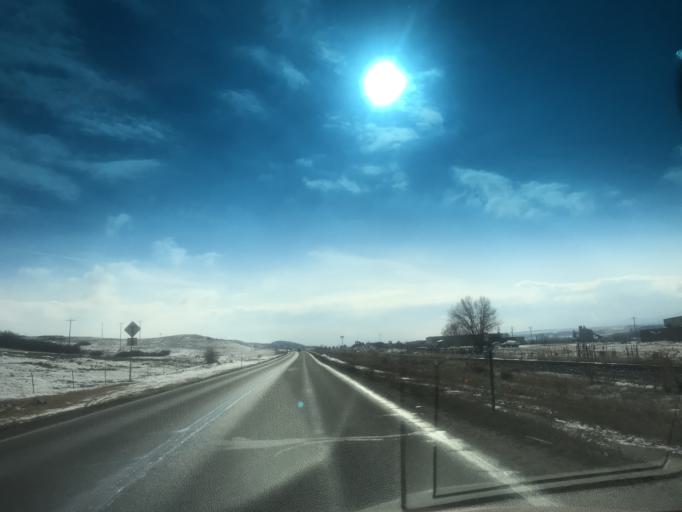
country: US
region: Colorado
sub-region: Douglas County
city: Highlands Ranch
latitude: 39.4780
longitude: -104.9923
